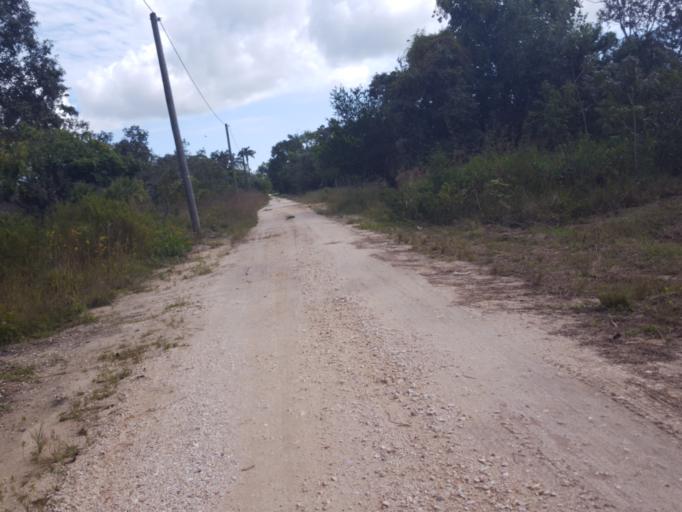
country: BZ
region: Belize
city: Belize City
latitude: 17.5709
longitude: -88.4079
